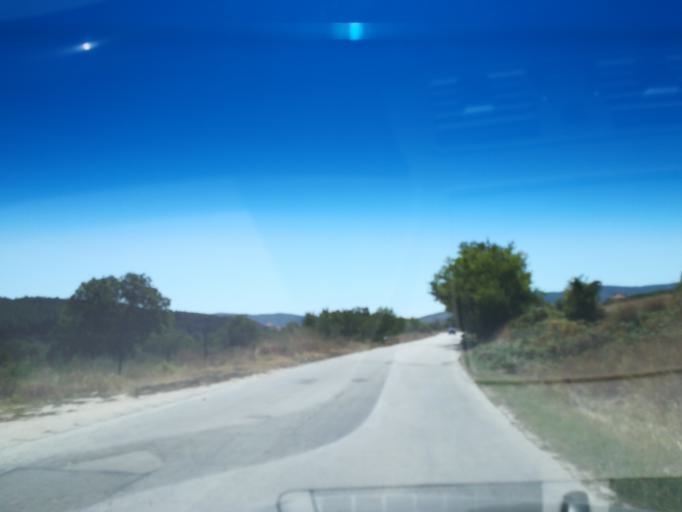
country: BG
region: Pazardzhik
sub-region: Obshtina Strelcha
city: Strelcha
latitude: 42.5181
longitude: 24.3224
